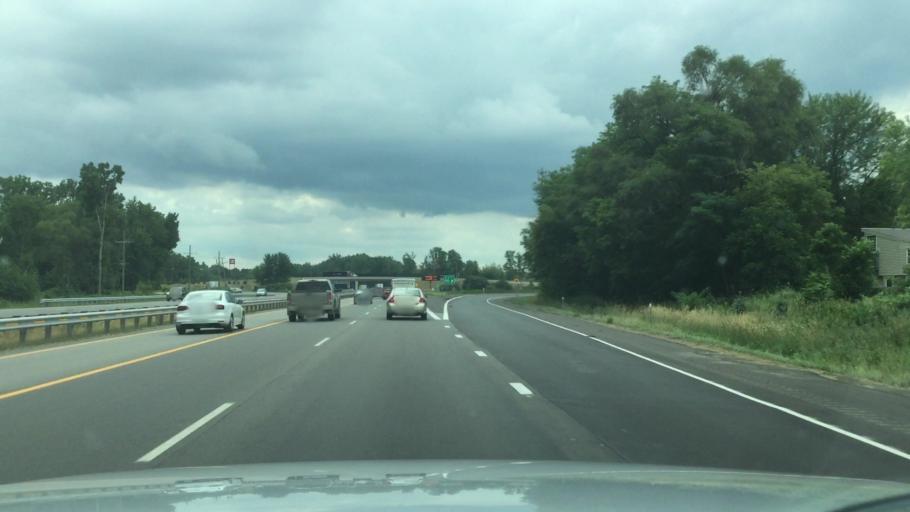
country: US
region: Michigan
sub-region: Livingston County
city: Whitmore Lake
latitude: 42.3990
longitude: -83.7634
